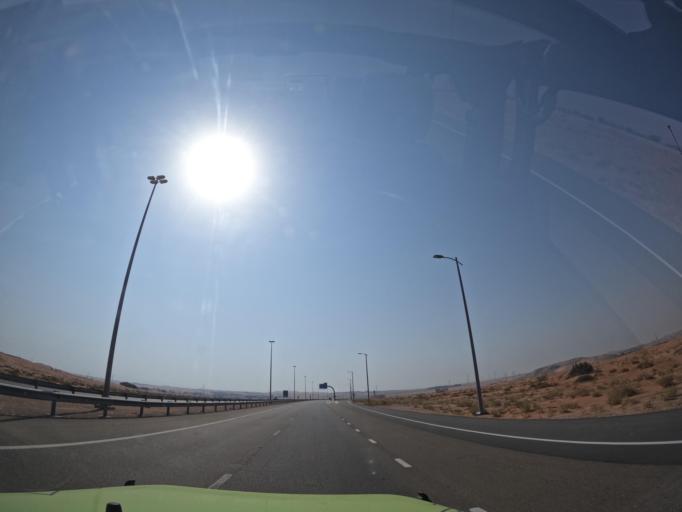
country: OM
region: Al Buraimi
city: Al Buraymi
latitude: 24.3967
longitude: 55.7187
